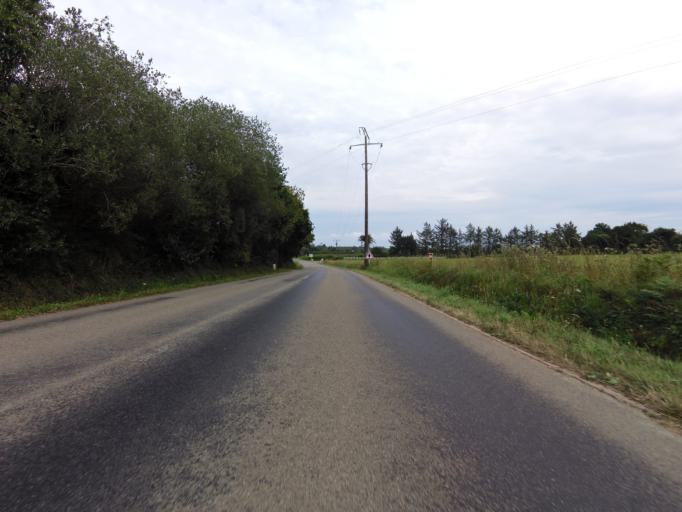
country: FR
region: Brittany
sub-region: Departement du Finistere
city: Poullan-sur-Mer
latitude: 48.0744
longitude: -4.4591
